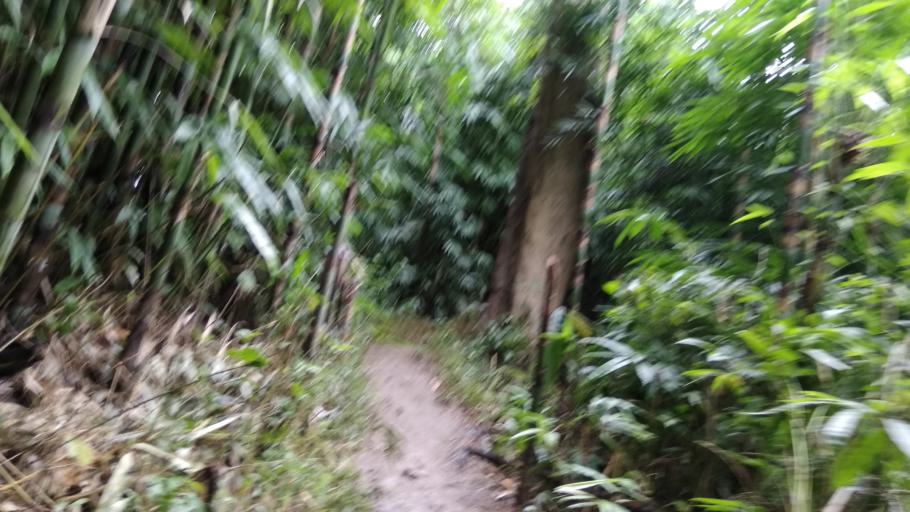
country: IN
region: Tripura
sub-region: Dhalai
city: Kamalpur
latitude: 24.1695
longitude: 91.9025
